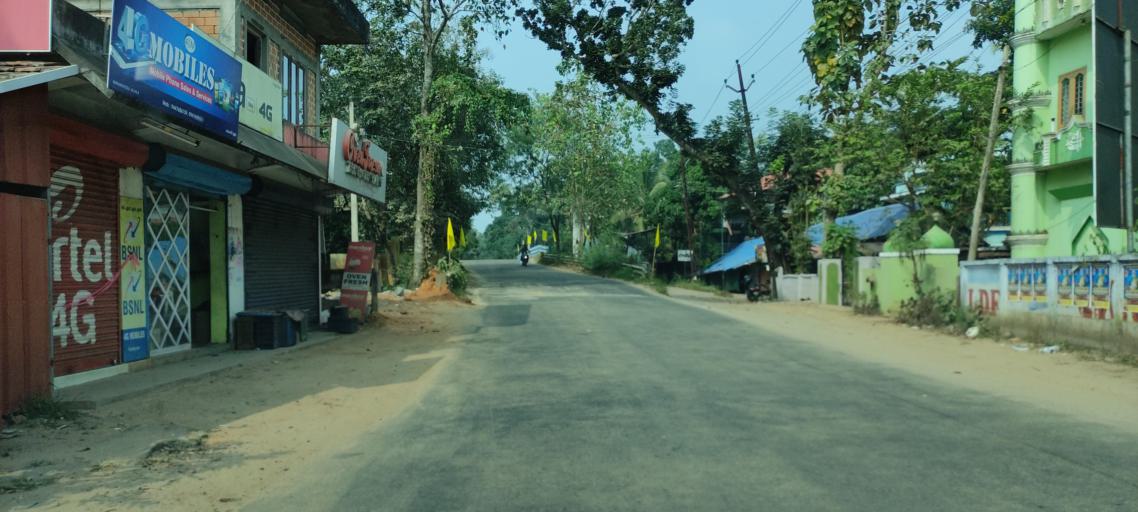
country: IN
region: Kerala
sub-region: Kottayam
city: Vaikam
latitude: 9.7235
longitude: 76.4157
